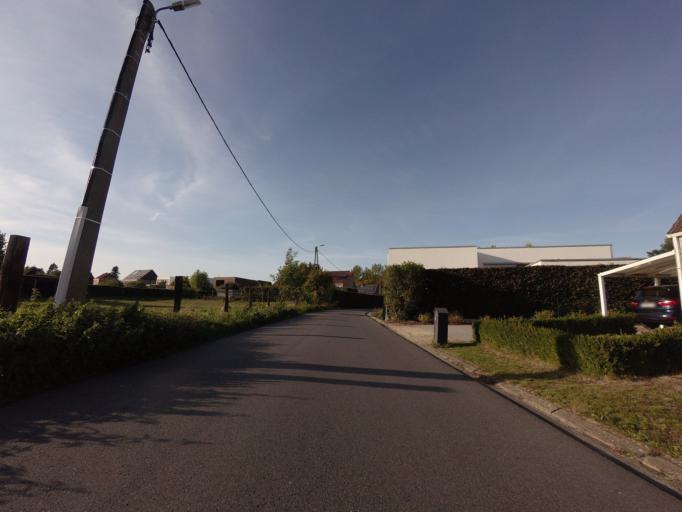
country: BE
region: Flanders
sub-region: Provincie Vlaams-Brabant
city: Kampenhout
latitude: 50.9445
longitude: 4.5776
